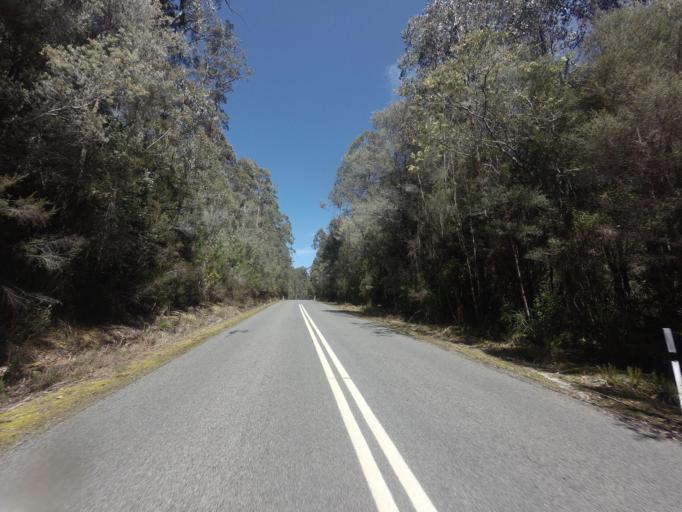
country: AU
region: Tasmania
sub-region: Huon Valley
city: Geeveston
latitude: -42.8281
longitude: 146.2716
